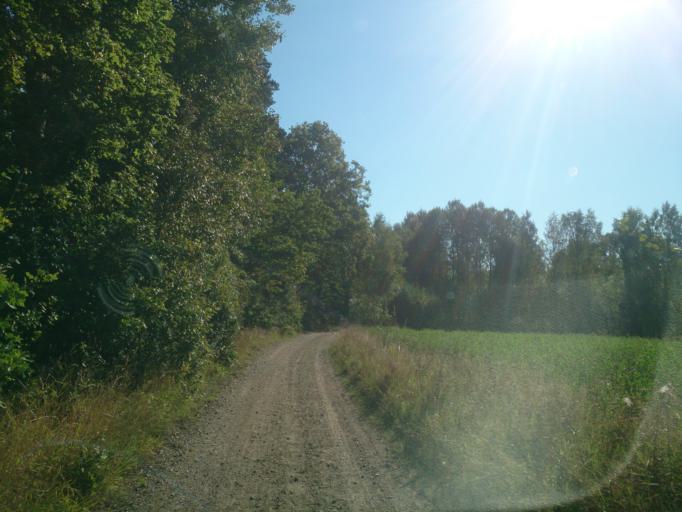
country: SE
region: OEstergoetland
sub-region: Atvidabergs Kommun
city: Atvidaberg
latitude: 58.2212
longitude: 15.9762
